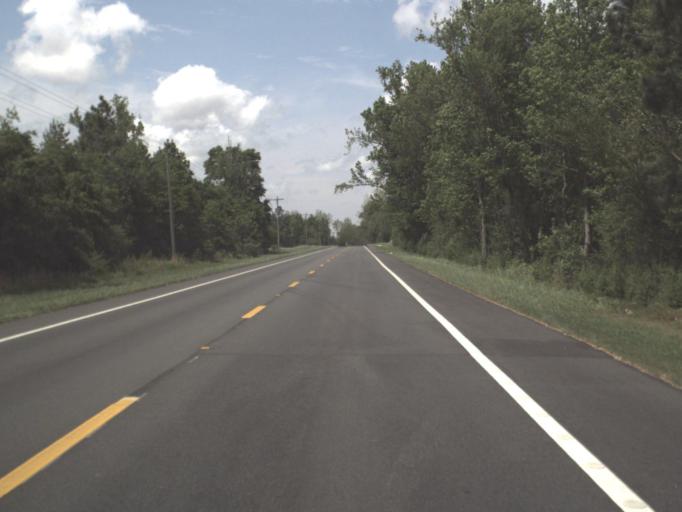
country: US
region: Florida
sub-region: Escambia County
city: Century
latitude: 30.8587
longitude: -87.1529
